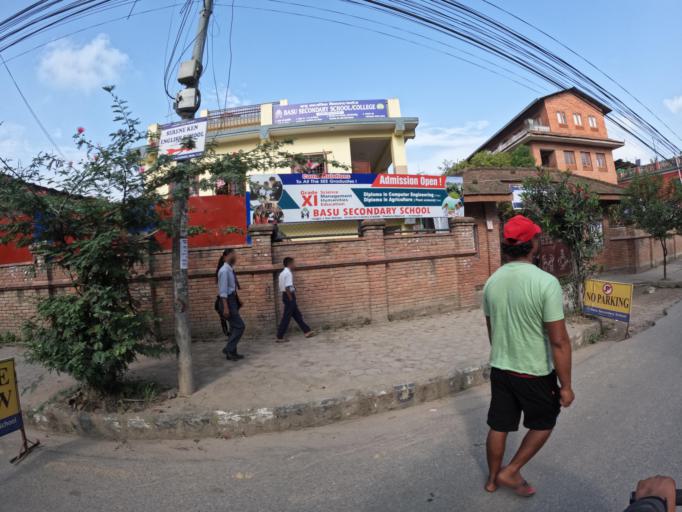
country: NP
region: Central Region
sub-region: Bagmati Zone
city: Bhaktapur
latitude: 27.6783
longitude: 85.4297
